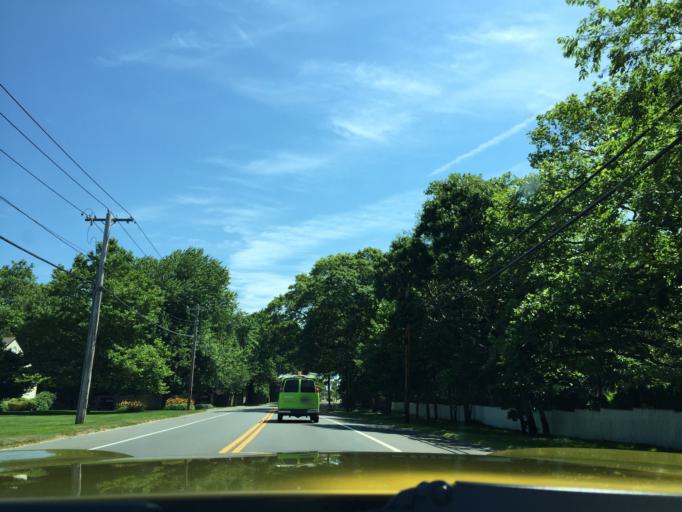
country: US
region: New York
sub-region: Suffolk County
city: Bridgehampton
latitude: 40.9465
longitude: -72.2530
